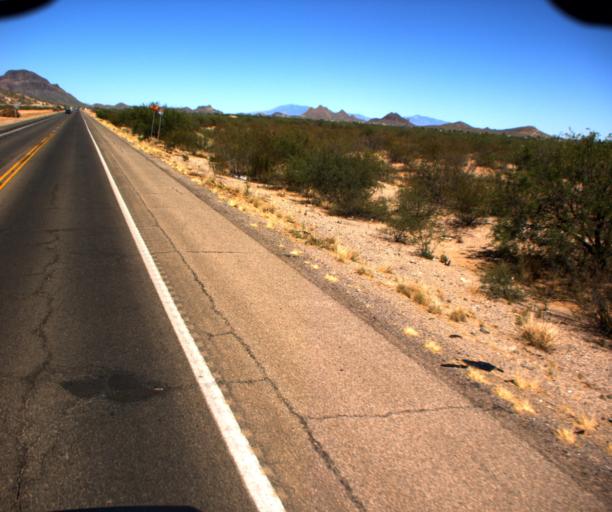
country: US
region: Arizona
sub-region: Pima County
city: Valencia West
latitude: 32.1501
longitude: -111.1257
